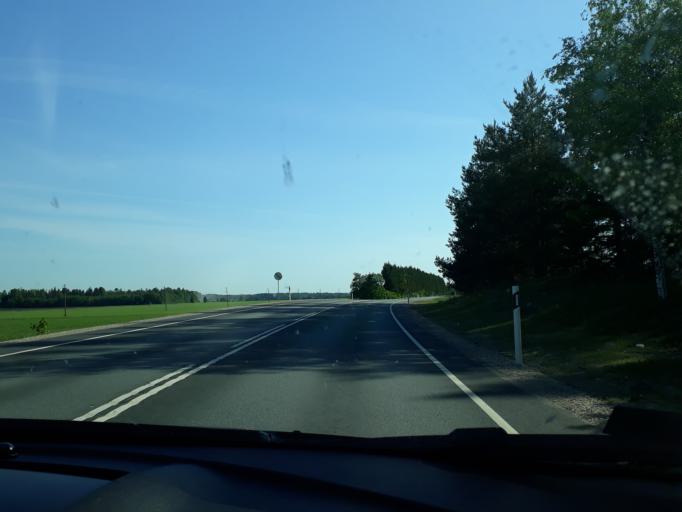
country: EE
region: Paernumaa
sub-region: Tootsi vald
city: Tootsi
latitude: 58.5455
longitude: 24.8461
